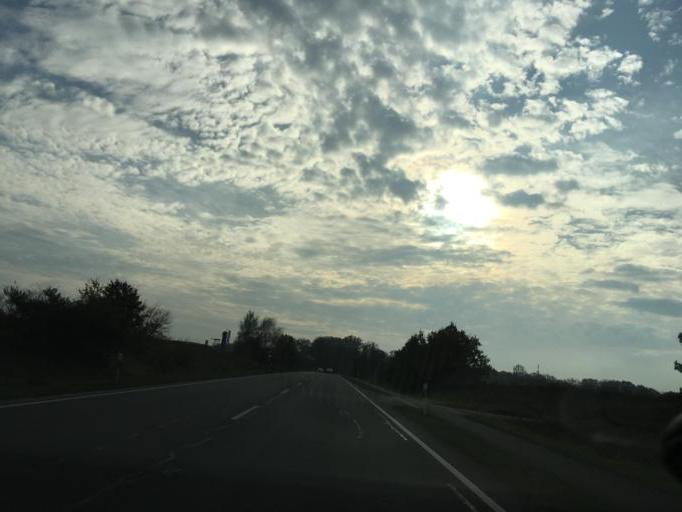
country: DE
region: Lower Saxony
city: Betzendorf
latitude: 53.1561
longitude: 10.2990
